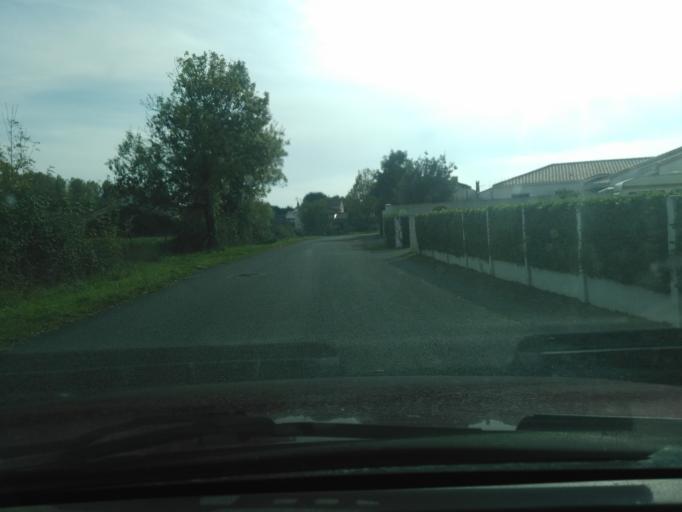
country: FR
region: Pays de la Loire
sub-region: Departement de la Vendee
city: Les Essarts
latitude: 46.7542
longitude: -1.2499
